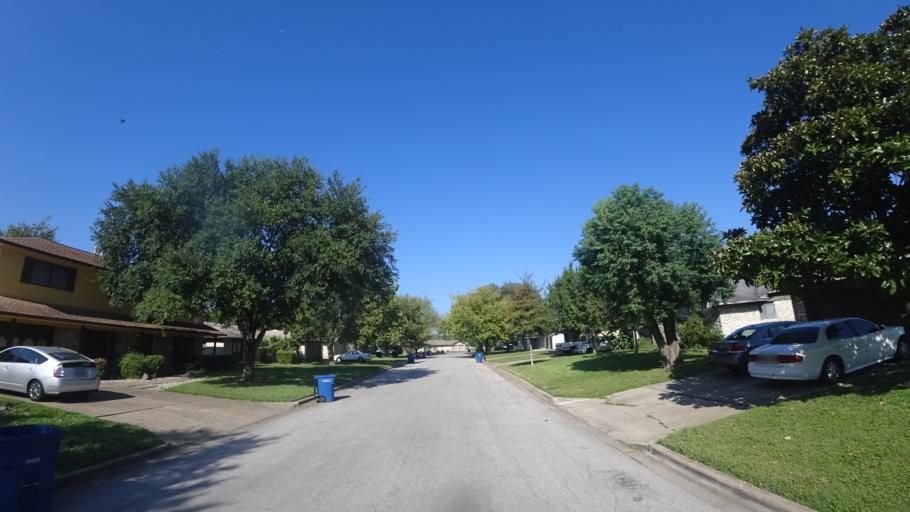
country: US
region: Texas
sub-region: Travis County
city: Austin
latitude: 30.3177
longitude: -97.6660
